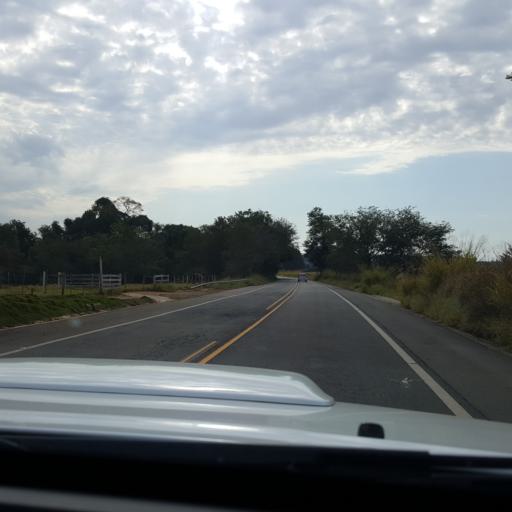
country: BR
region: Sao Paulo
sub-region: Itaporanga
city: Itaporanga
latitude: -23.7285
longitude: -49.4596
